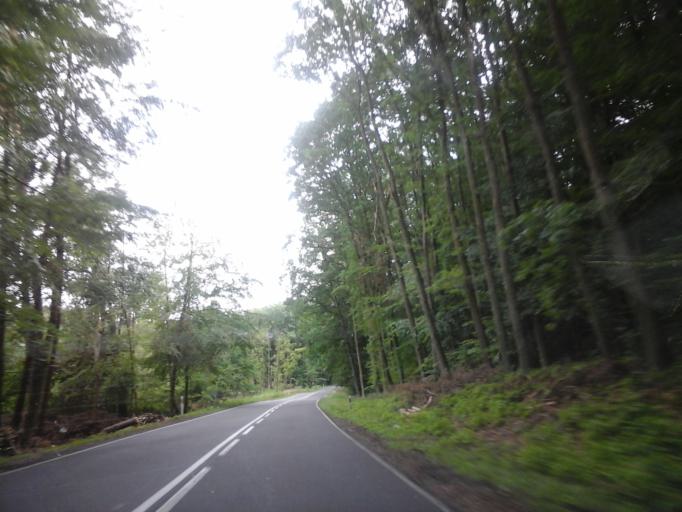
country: PL
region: West Pomeranian Voivodeship
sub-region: Powiat stargardzki
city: Suchan
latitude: 53.2711
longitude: 15.3287
